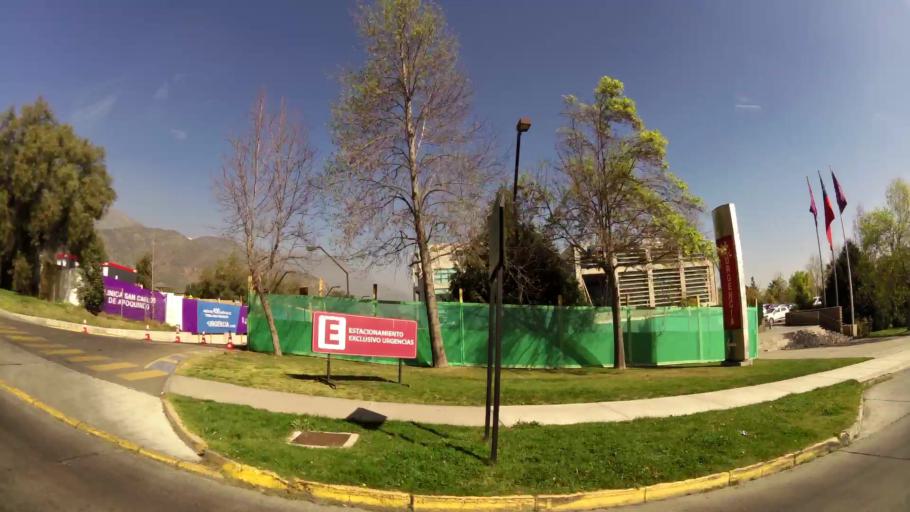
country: CL
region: Santiago Metropolitan
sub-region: Provincia de Santiago
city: Villa Presidente Frei, Nunoa, Santiago, Chile
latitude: -33.3996
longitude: -70.5094
